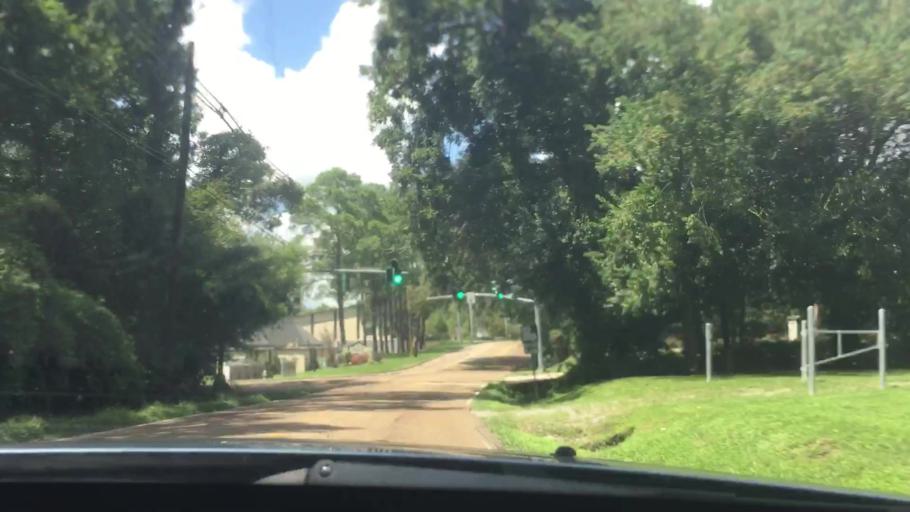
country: US
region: Louisiana
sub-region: East Baton Rouge Parish
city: Gardere
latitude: 30.3655
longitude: -91.1181
